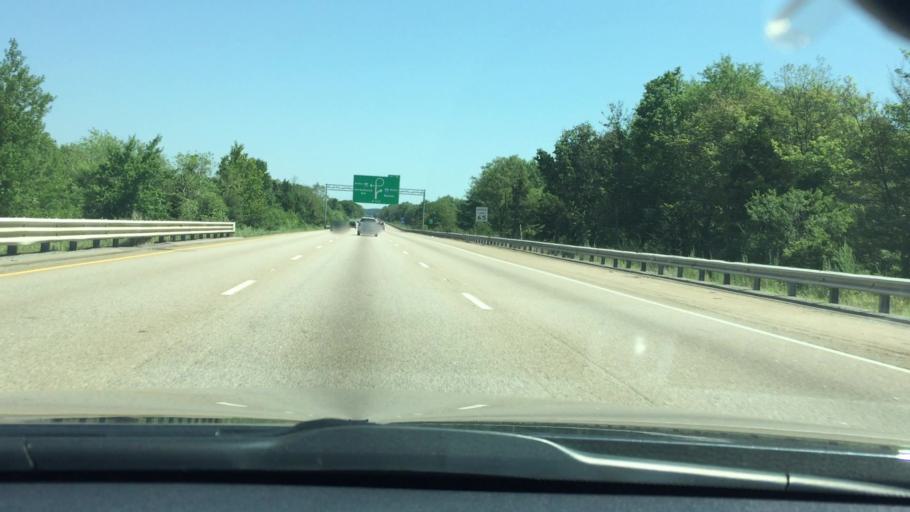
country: US
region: Massachusetts
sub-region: Norfolk County
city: Canton
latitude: 42.1758
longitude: -71.1663
